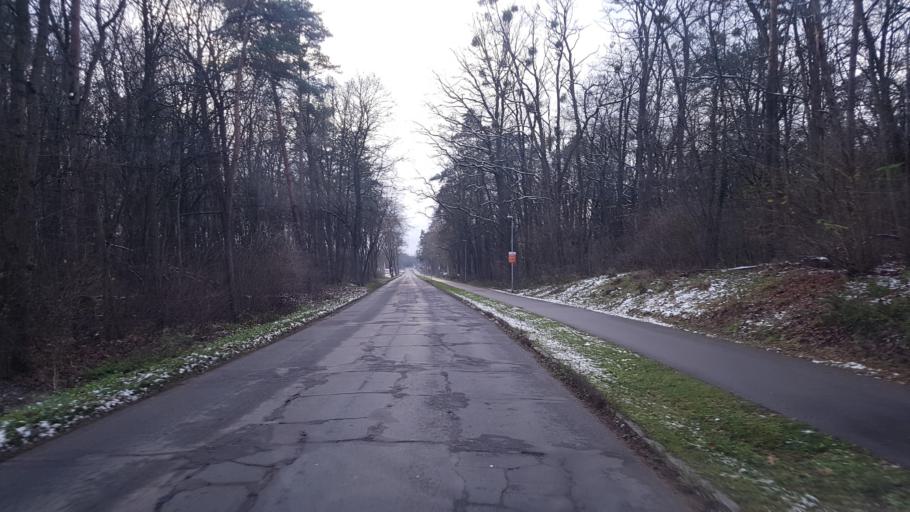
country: DE
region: Brandenburg
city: Petershagen
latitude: 52.5006
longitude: 13.8288
